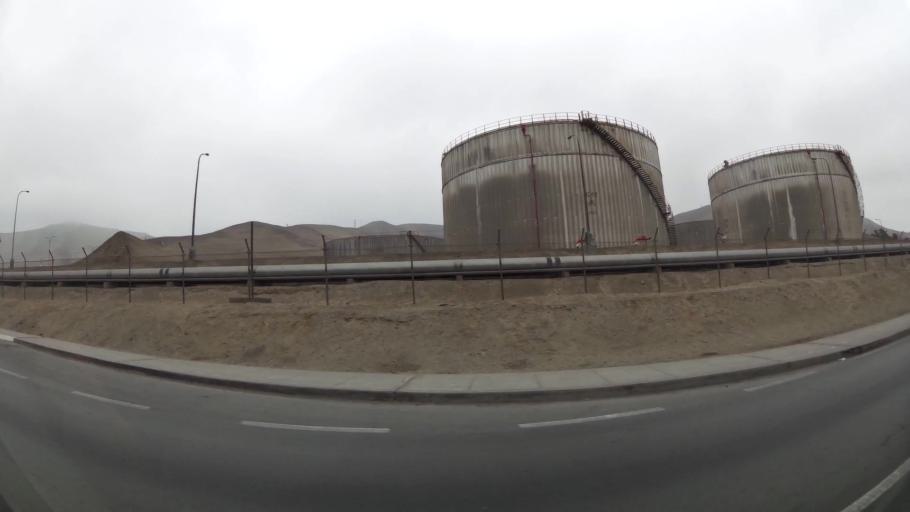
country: PE
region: Lima
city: Ventanilla
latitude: -11.9151
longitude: -77.1286
